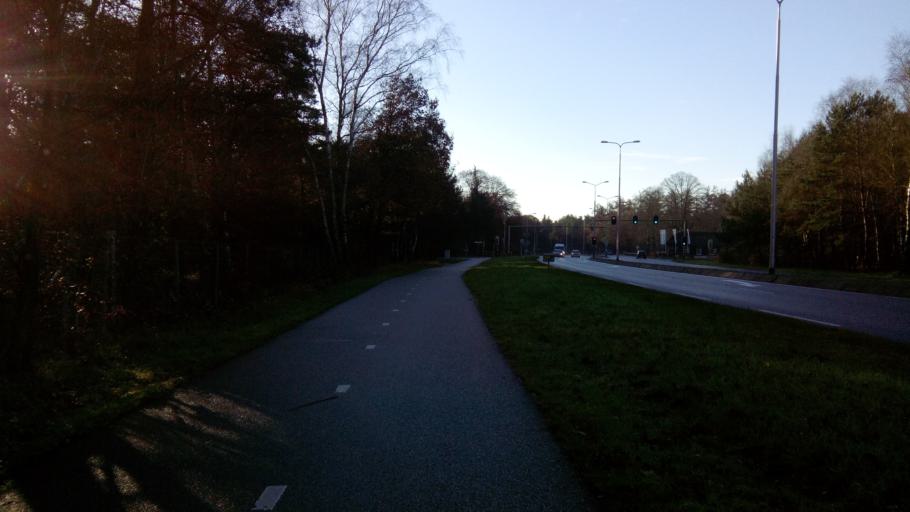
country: NL
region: Utrecht
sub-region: Gemeente Utrechtse Heuvelrug
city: Maarn
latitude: 52.0937
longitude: 5.3623
